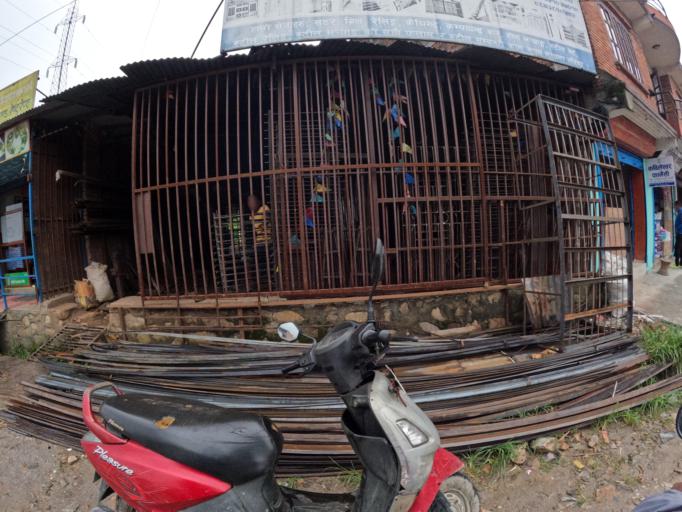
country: NP
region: Central Region
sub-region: Bagmati Zone
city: Kathmandu
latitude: 27.7629
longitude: 85.3189
